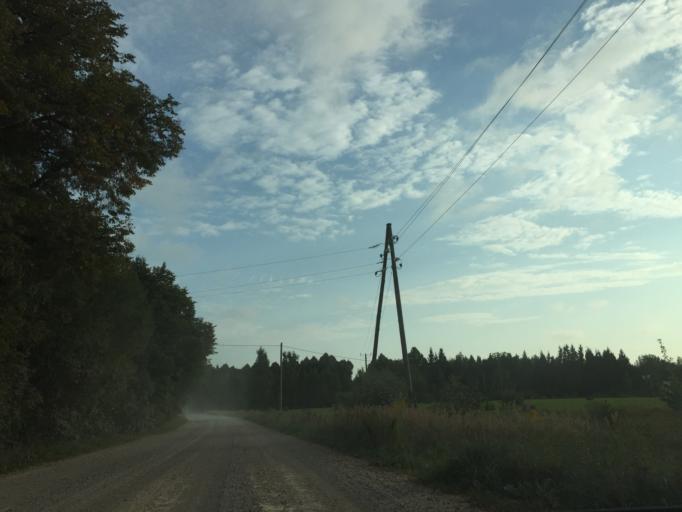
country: LV
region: Ikskile
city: Ikskile
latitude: 56.8136
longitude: 24.4478
